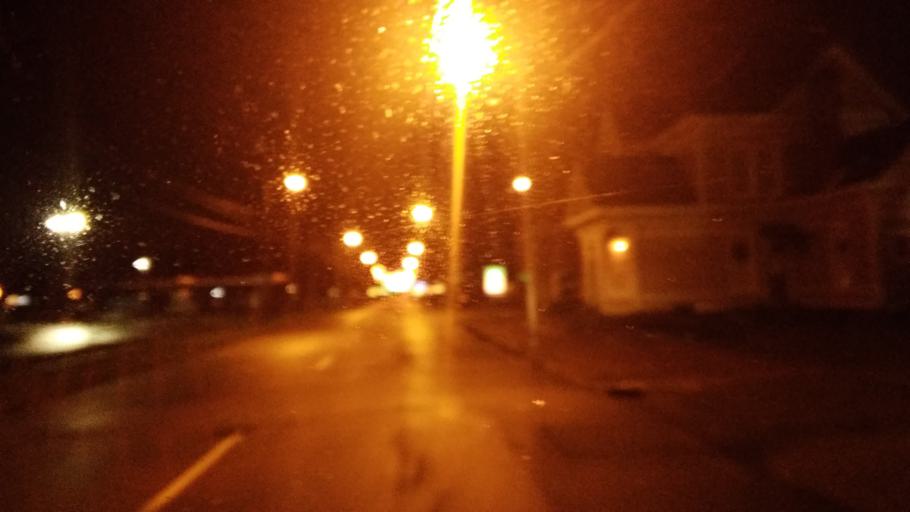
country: US
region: Ohio
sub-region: Scioto County
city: Portsmouth
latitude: 38.7358
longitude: -82.9944
